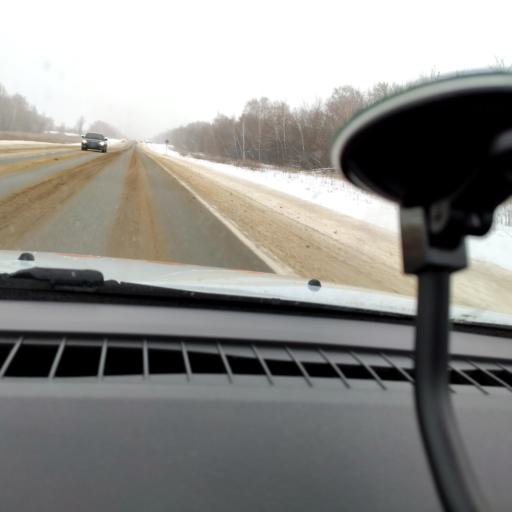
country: RU
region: Samara
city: Dubovyy Umet
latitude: 53.0343
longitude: 50.2145
